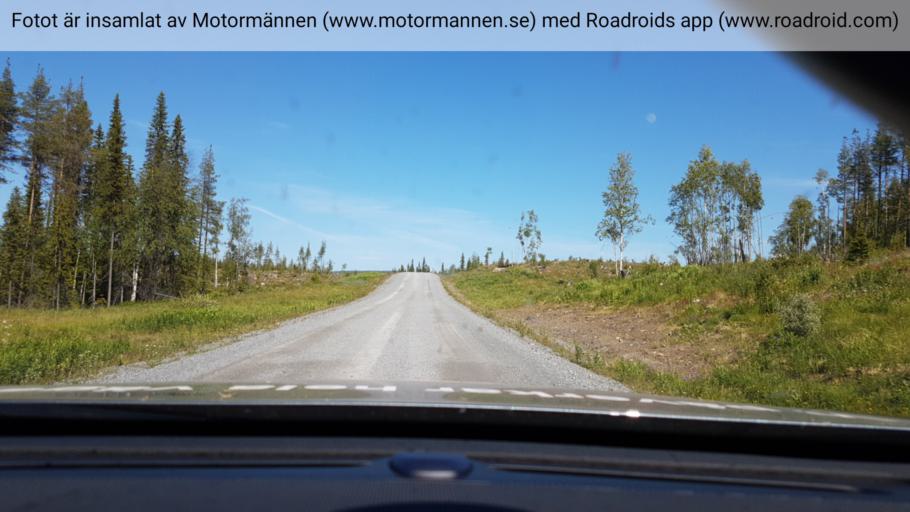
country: SE
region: Vaesterbotten
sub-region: Vilhelmina Kommun
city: Sjoberg
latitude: 64.6895
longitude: 15.7552
